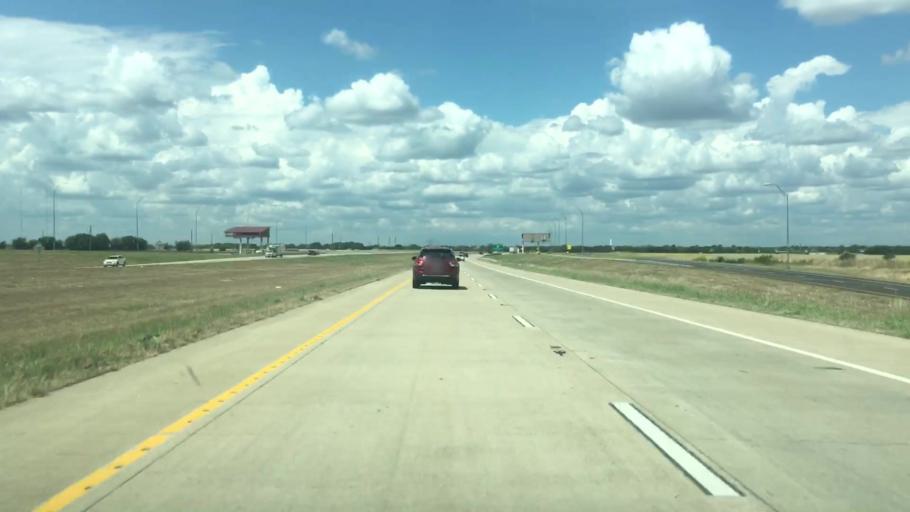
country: US
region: Texas
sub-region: Williamson County
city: Georgetown
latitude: 30.6224
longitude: -97.6177
